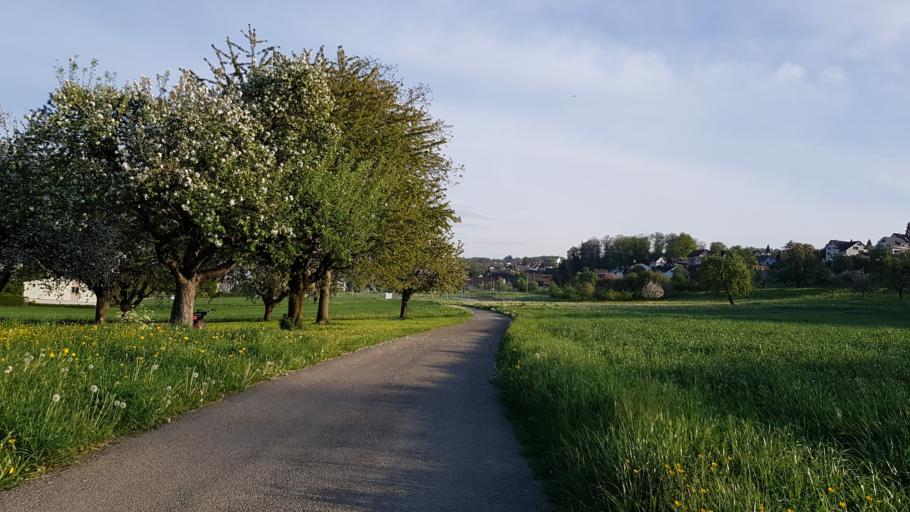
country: CH
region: Aargau
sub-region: Bezirk Kulm
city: Reinach
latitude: 47.2734
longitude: 8.2074
